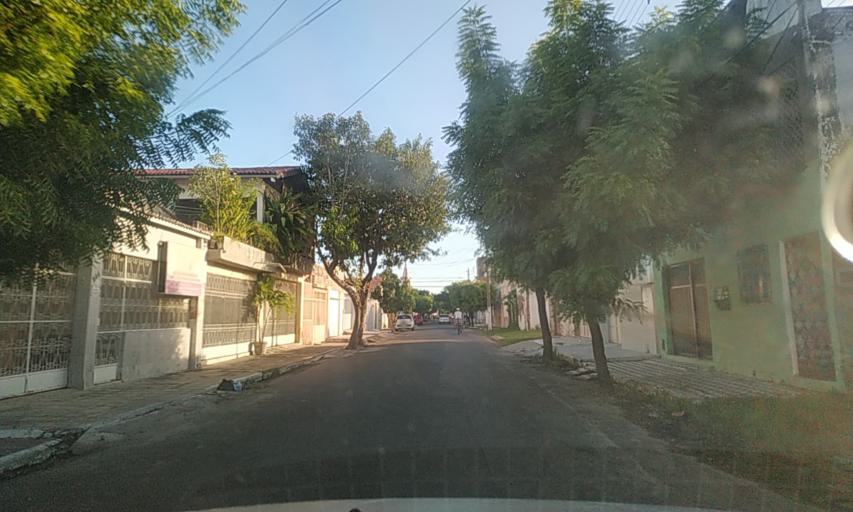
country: BR
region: Rio Grande do Norte
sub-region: Mossoro
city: Mossoro
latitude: -5.1916
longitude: -37.3385
